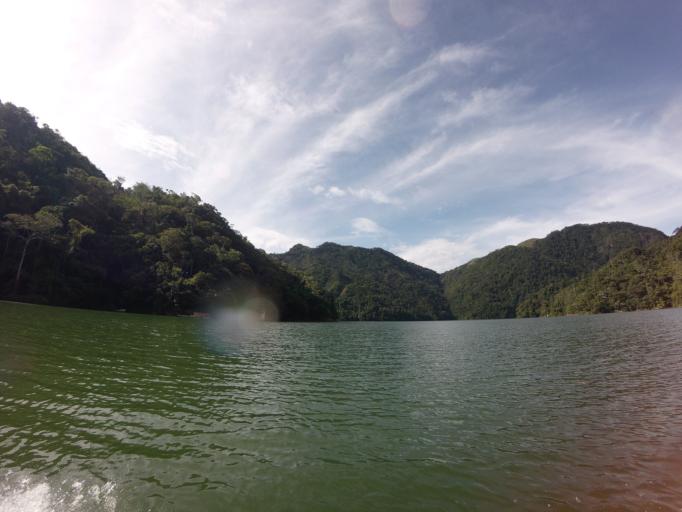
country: CO
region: Caldas
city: Norcasia
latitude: 5.5592
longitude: -74.9079
